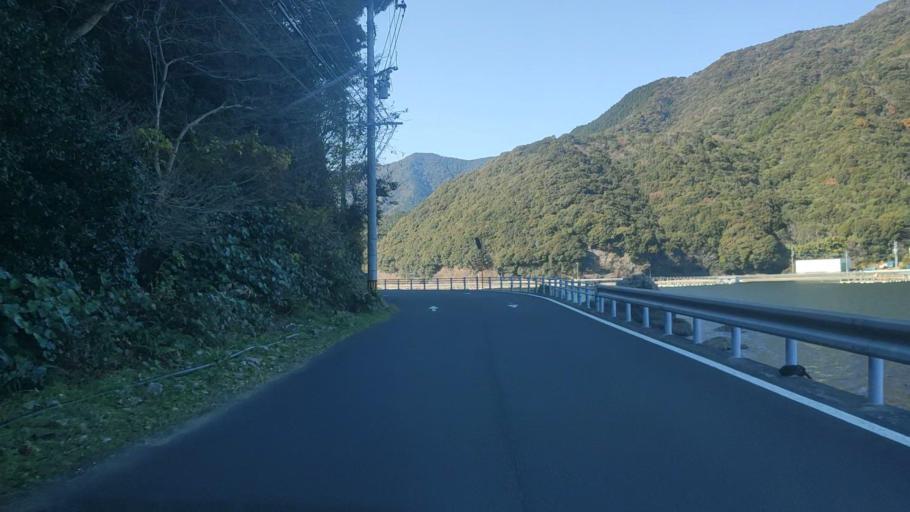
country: JP
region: Oita
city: Saiki
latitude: 32.8364
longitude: 131.9544
